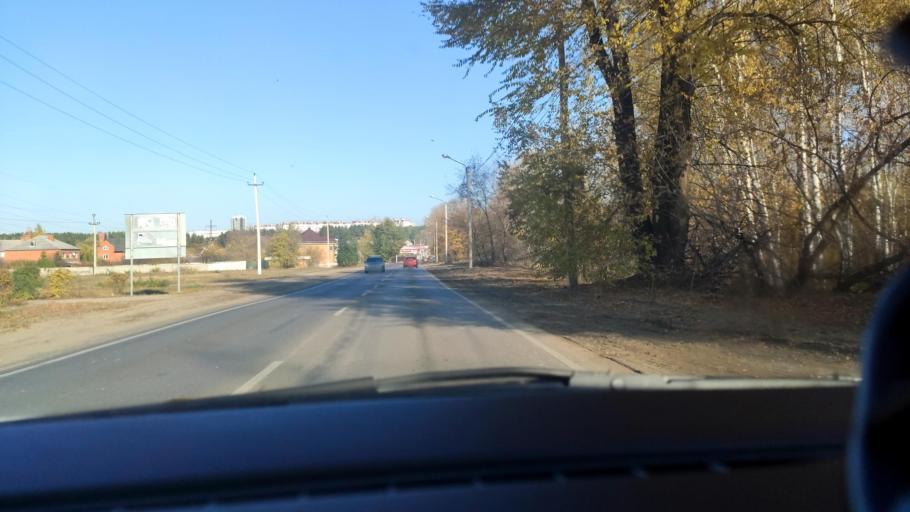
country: RU
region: Voronezj
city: Pridonskoy
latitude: 51.6423
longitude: 39.0932
